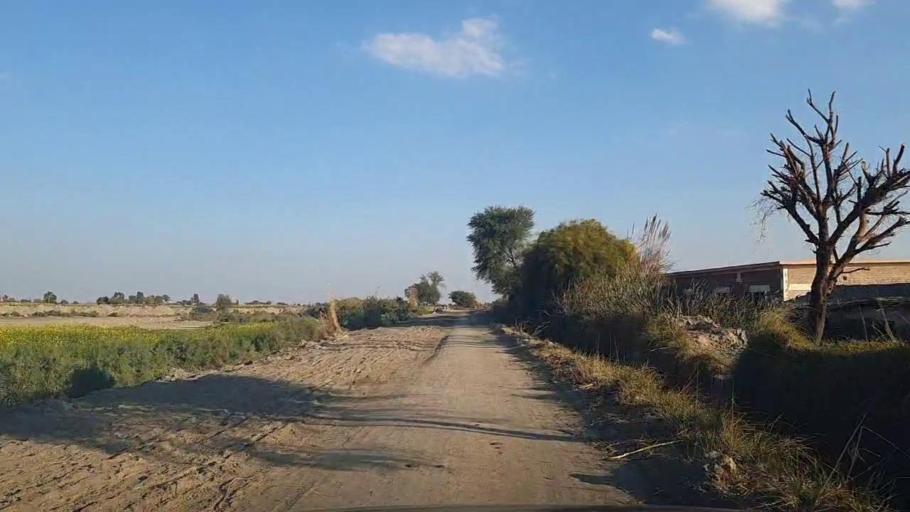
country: PK
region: Sindh
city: Jhol
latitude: 25.9202
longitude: 69.0393
